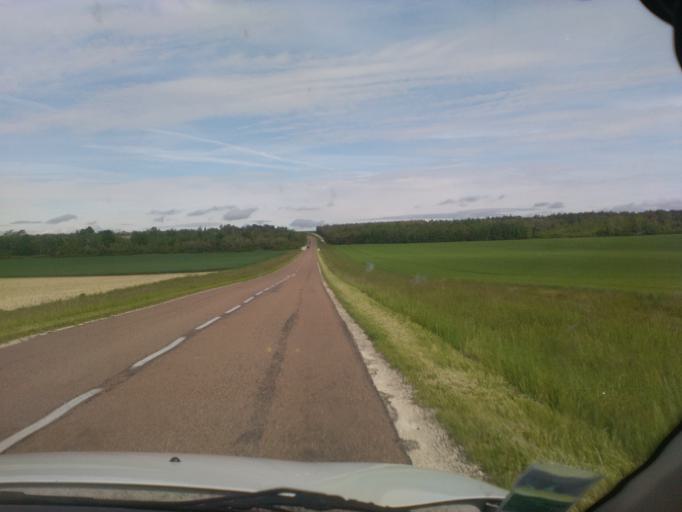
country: FR
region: Champagne-Ardenne
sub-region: Departement de l'Aube
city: Payns
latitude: 48.3774
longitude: 3.8786
